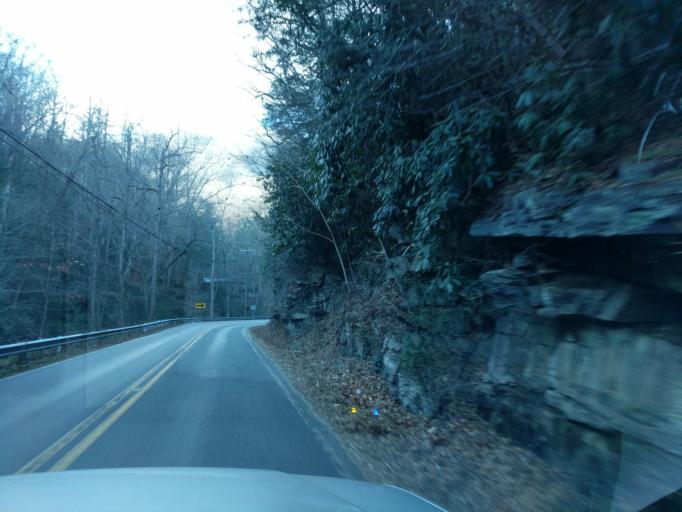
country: US
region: North Carolina
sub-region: Henderson County
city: Edneyville
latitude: 35.4523
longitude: -82.2961
